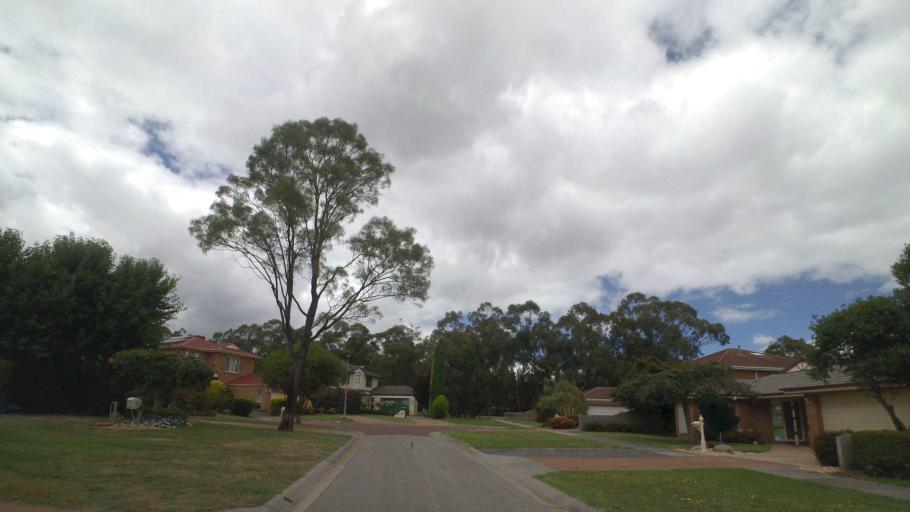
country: AU
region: Victoria
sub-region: Knox
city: The Basin
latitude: -37.8405
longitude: 145.3084
